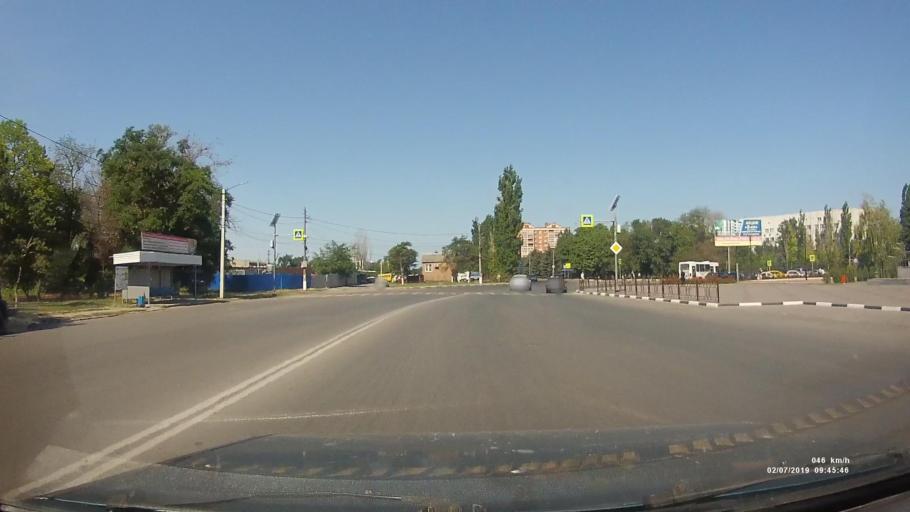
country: RU
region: Rostov
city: Azov
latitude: 47.1019
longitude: 39.4107
